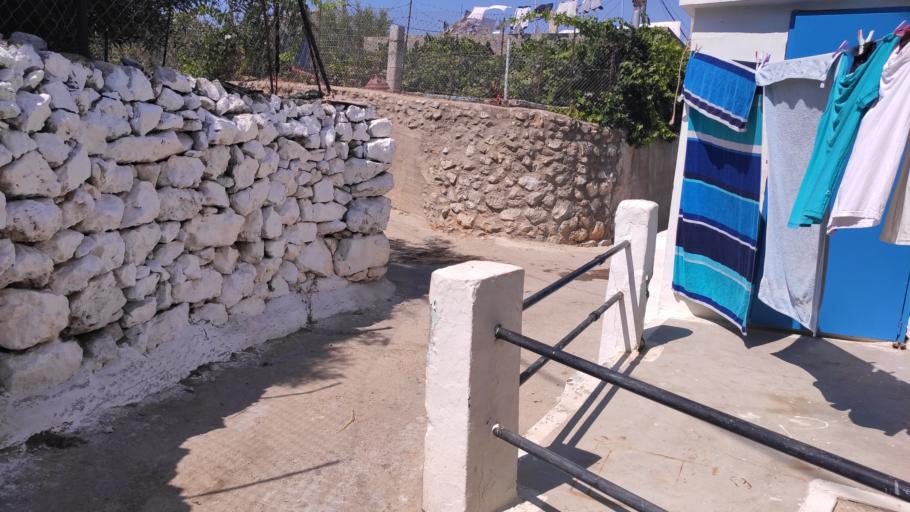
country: GR
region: South Aegean
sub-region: Nomos Dodekanisou
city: Pylion
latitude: 36.9322
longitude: 27.1351
